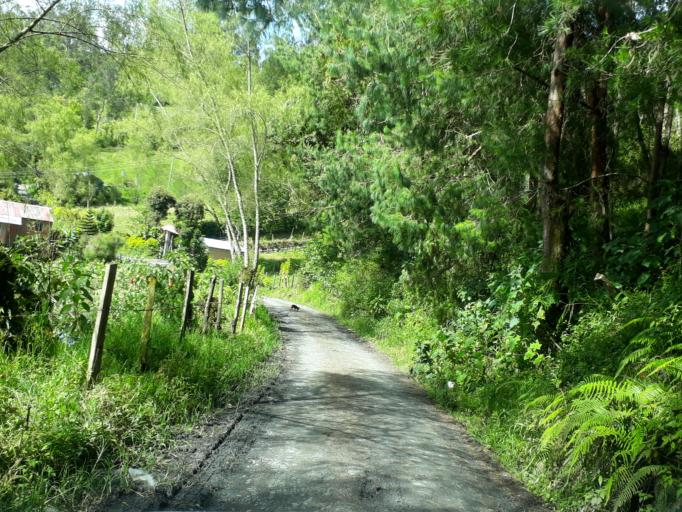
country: CO
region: Cundinamarca
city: Junin
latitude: 4.7525
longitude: -73.6349
